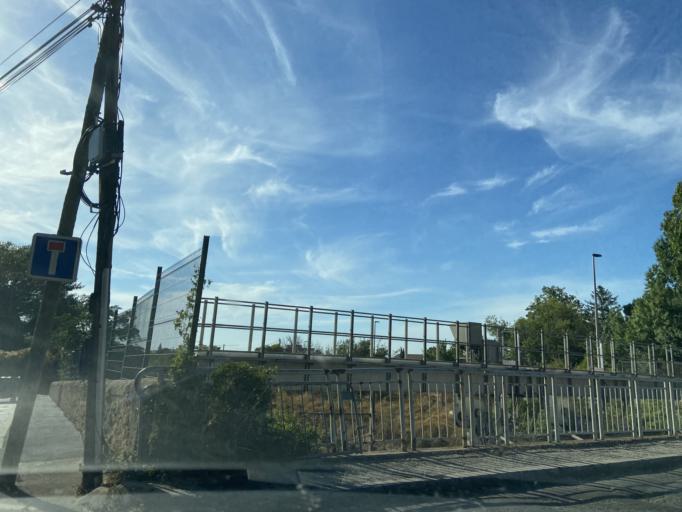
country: FR
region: Provence-Alpes-Cote d'Azur
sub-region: Departement des Bouches-du-Rhone
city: Miramas
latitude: 43.5797
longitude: 5.0085
